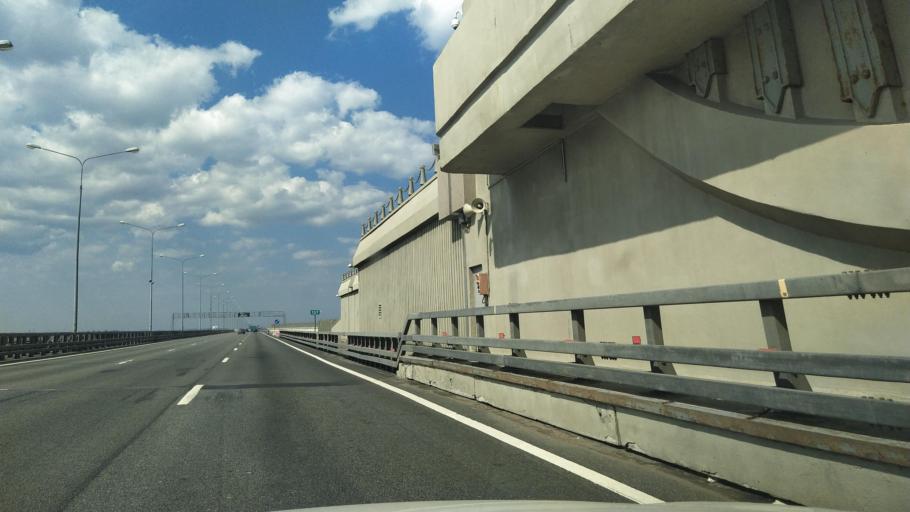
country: RU
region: Leningrad
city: Gorskaya
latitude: 60.0328
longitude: 29.9033
